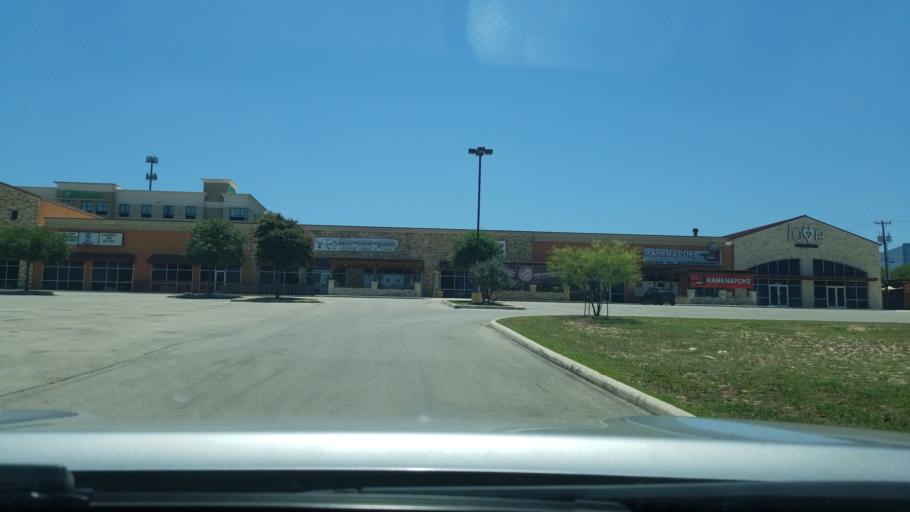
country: US
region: Texas
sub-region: Bexar County
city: Hollywood Park
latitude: 29.6218
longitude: -98.4633
